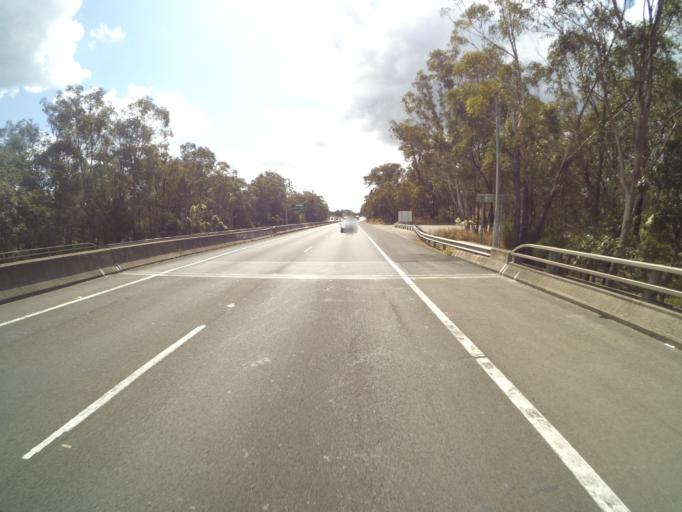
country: AU
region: New South Wales
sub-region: Wollondilly
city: Douglas Park
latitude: -34.2367
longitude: 150.6628
